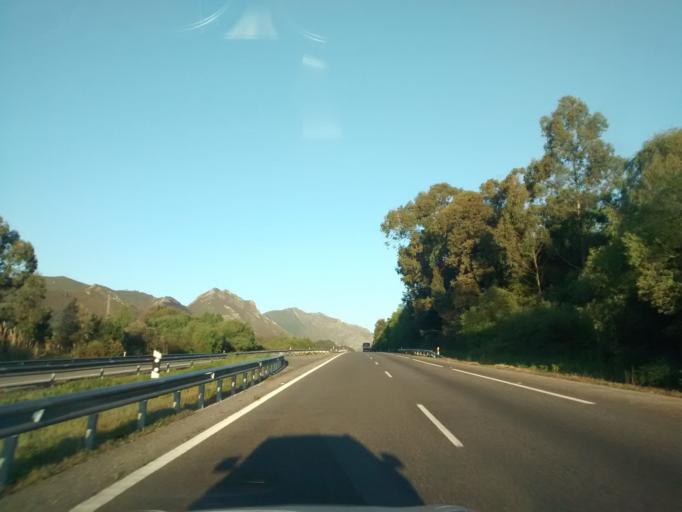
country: ES
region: Asturias
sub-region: Province of Asturias
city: Ribadesella
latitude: 43.4451
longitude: -4.9262
